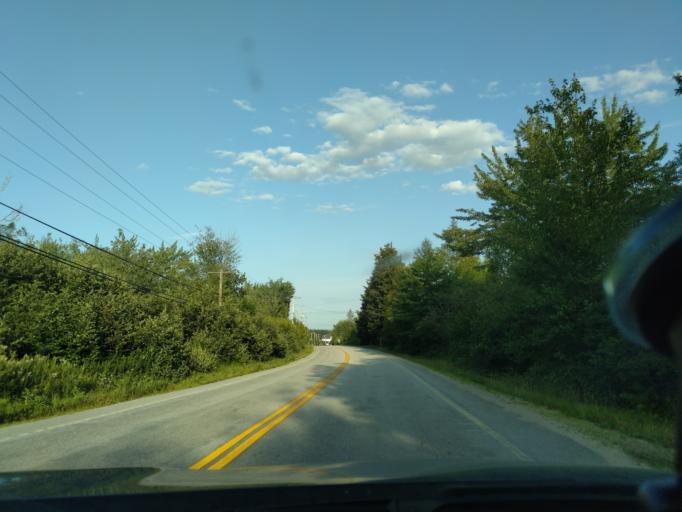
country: US
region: Maine
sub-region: Hancock County
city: Gouldsboro
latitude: 44.3913
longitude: -68.0483
